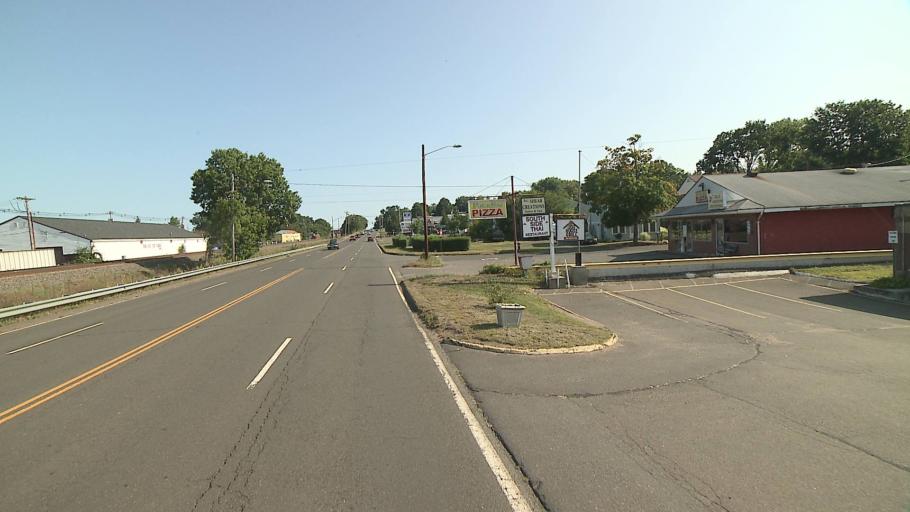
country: US
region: Connecticut
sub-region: New Haven County
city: Wallingford Center
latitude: 41.4417
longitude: -72.8314
